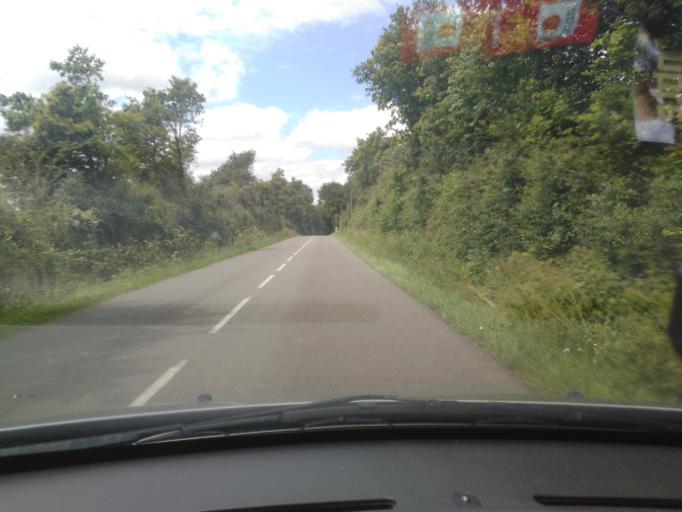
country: FR
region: Pays de la Loire
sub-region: Departement de la Vendee
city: Chauche
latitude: 46.7850
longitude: -1.2885
